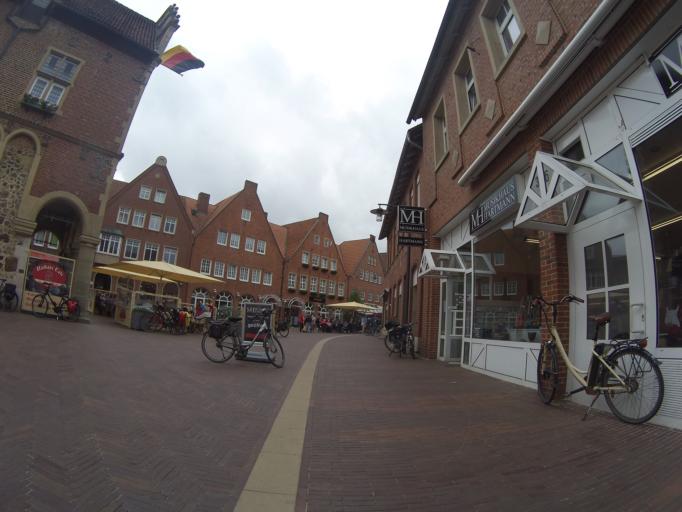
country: DE
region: Lower Saxony
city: Meppen
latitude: 52.6911
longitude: 7.2921
